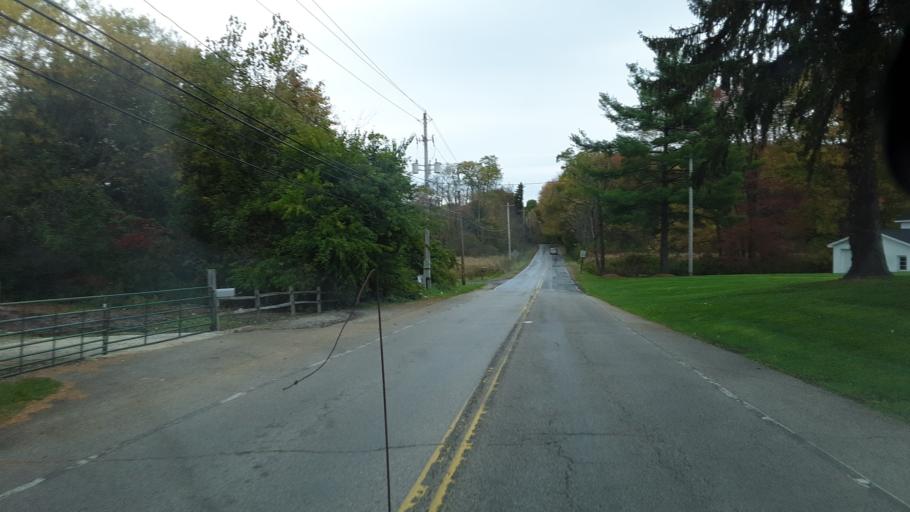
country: US
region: Ohio
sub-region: Portage County
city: Kent
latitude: 41.1301
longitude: -81.3508
